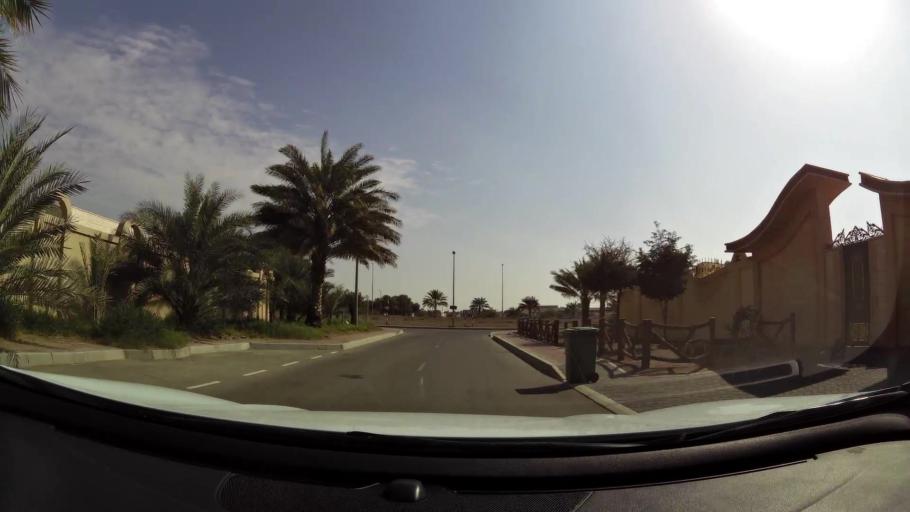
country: AE
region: Abu Dhabi
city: Al Ain
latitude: 24.0952
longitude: 55.9231
